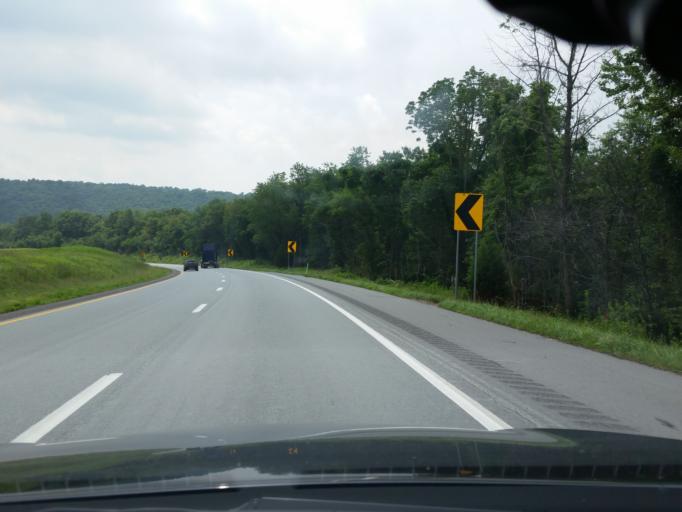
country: US
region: Pennsylvania
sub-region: Perry County
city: Newport
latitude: 40.4812
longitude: -77.0721
